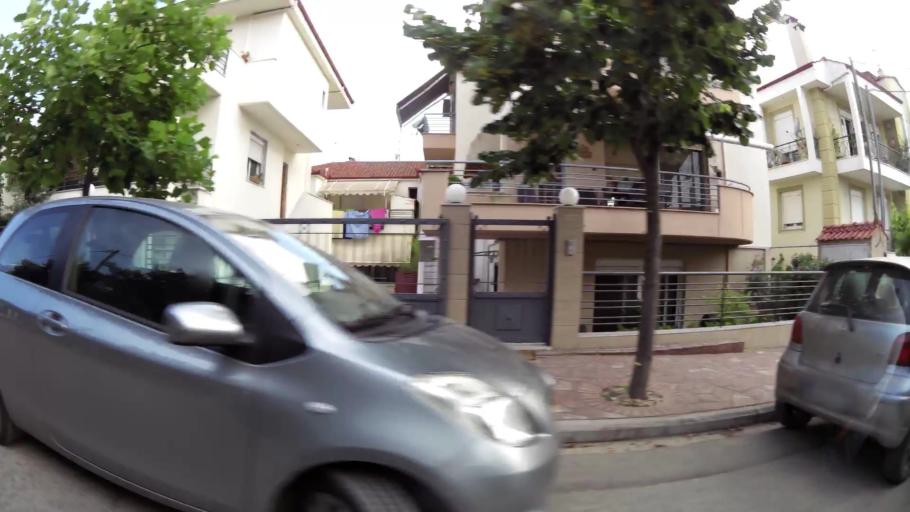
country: GR
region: Central Macedonia
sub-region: Nomos Thessalonikis
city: Pefka
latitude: 40.6593
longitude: 22.9837
